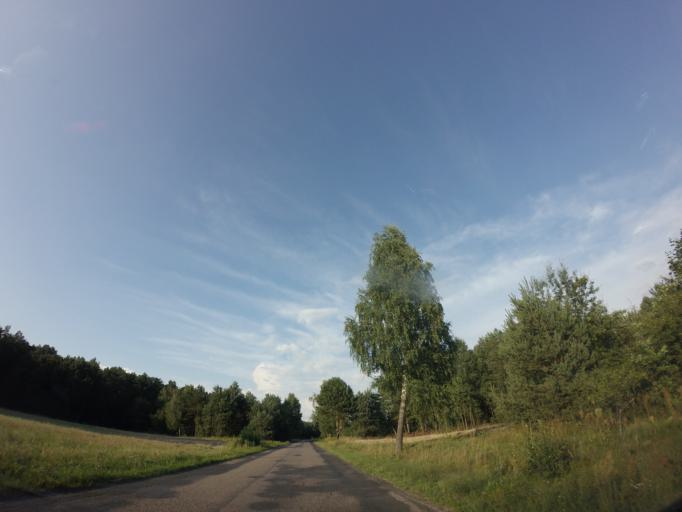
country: PL
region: Lublin Voivodeship
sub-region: Powiat pulawski
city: Kurow
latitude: 51.4272
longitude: 22.2088
